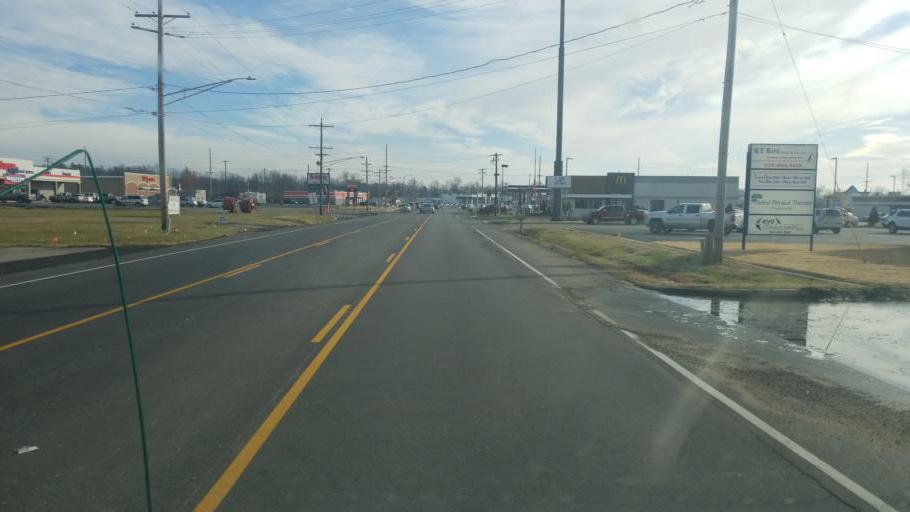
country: US
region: Missouri
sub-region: Stoddard County
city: Dexter
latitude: 36.8037
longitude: -89.9729
